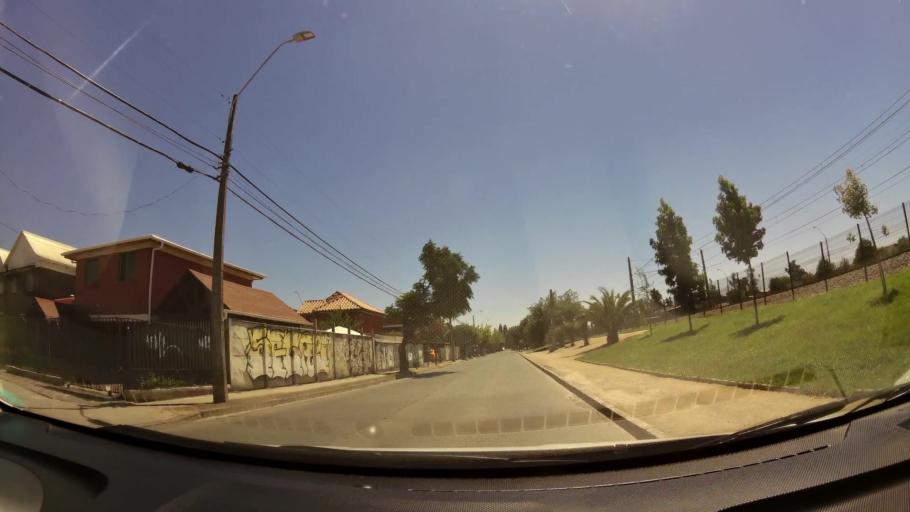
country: CL
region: O'Higgins
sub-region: Provincia de Cachapoal
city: Rancagua
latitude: -34.1579
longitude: -70.7499
